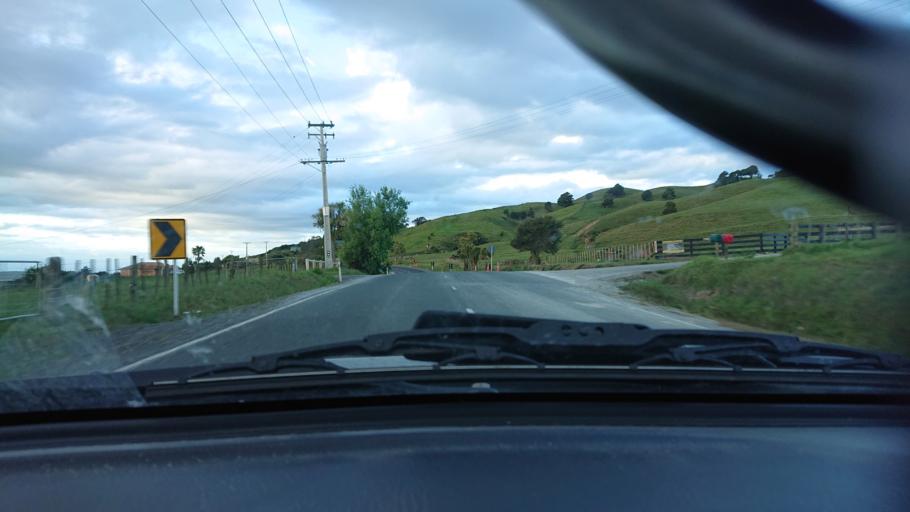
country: NZ
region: Auckland
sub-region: Auckland
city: Wellsford
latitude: -36.4491
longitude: 174.4334
